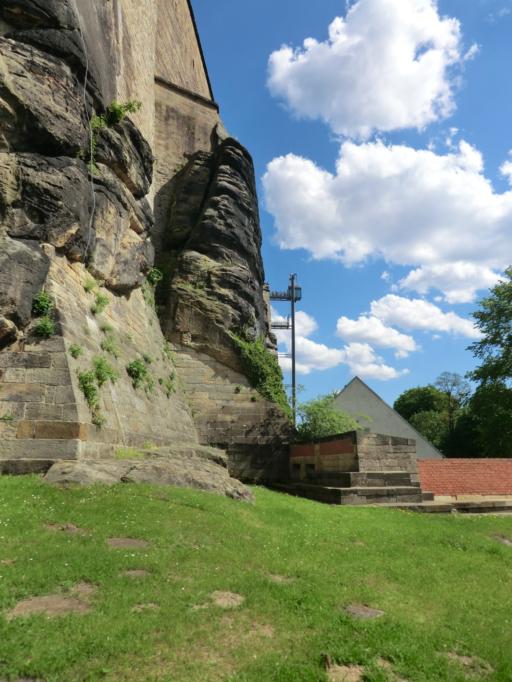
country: DE
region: Saxony
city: Konigstein
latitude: 50.9190
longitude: 14.0545
